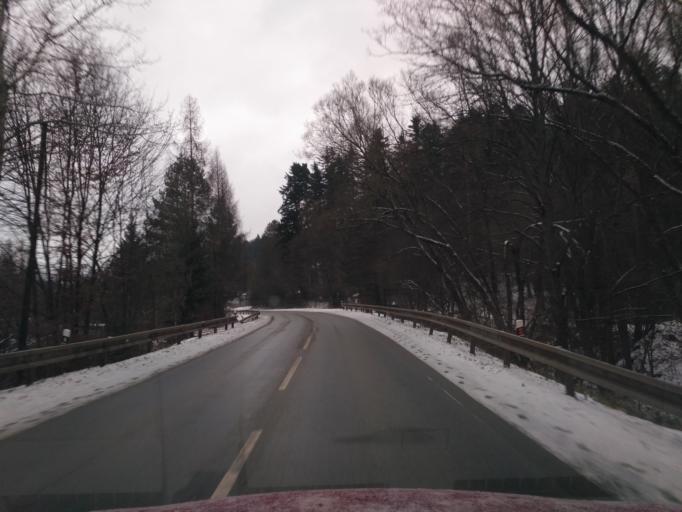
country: SK
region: Presovsky
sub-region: Okres Presov
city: Presov
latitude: 48.9807
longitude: 21.1745
